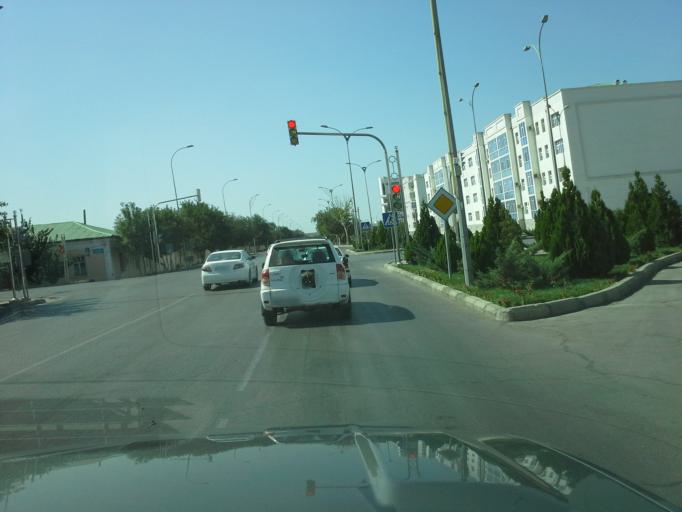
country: TM
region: Dasoguz
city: Dasoguz
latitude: 41.8387
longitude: 59.9498
